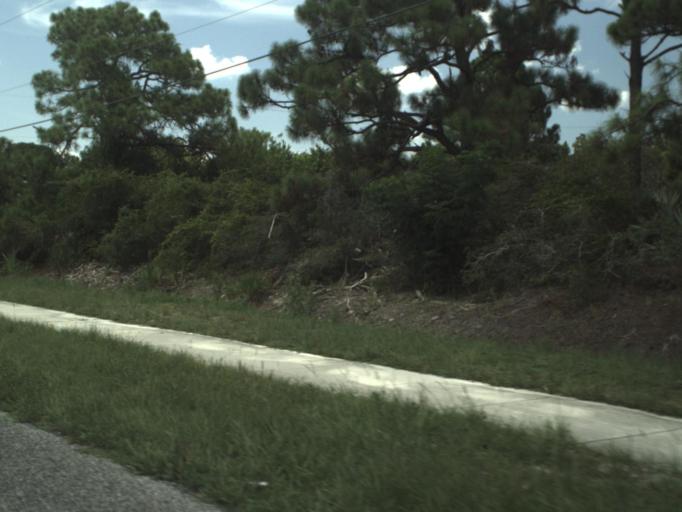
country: US
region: Florida
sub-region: Martin County
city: Port Salerno
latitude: 27.1078
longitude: -80.1682
